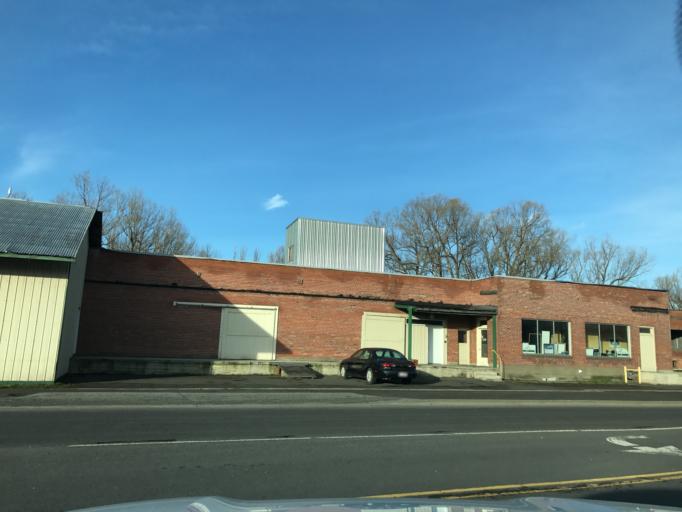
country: US
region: Idaho
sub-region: Latah County
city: Moscow
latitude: 46.7254
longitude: -116.9987
